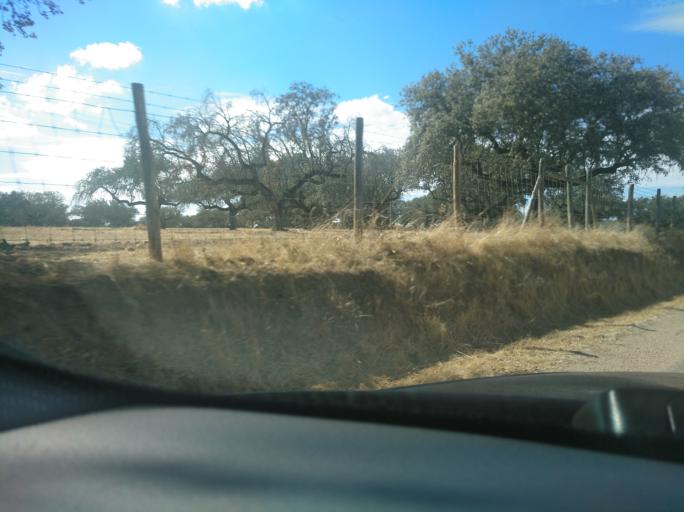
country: ES
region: Extremadura
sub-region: Provincia de Badajoz
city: La Codosera
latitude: 39.1308
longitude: -7.1565
